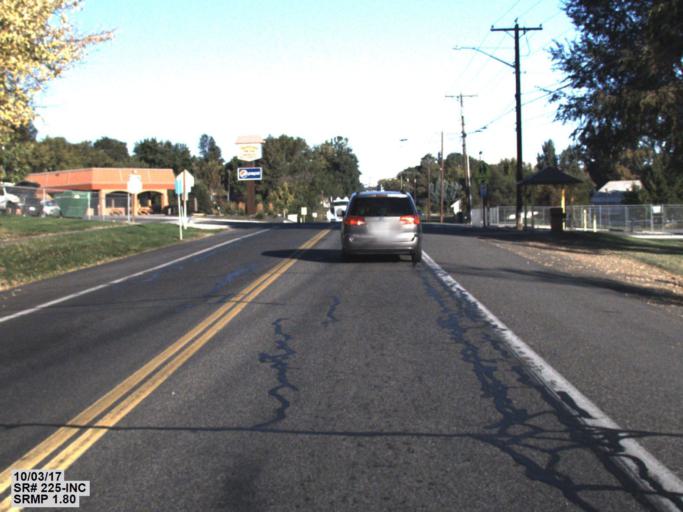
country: US
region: Washington
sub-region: Benton County
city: Benton City
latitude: 46.2707
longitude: -119.4885
